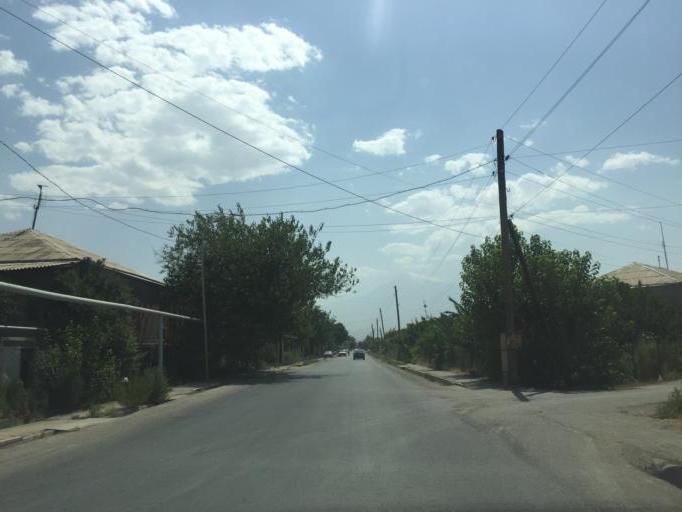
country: AM
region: Ararat
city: Aralez
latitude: 39.9051
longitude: 44.6053
